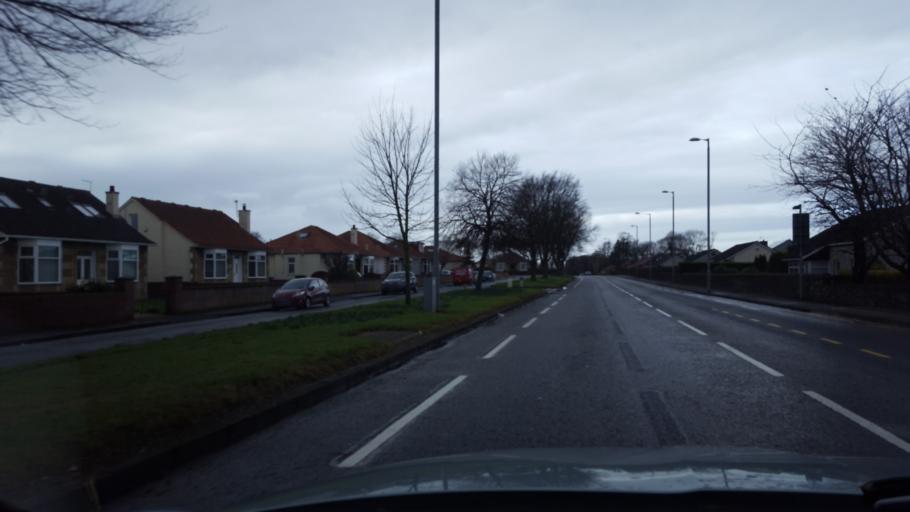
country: GB
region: Scotland
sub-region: South Ayrshire
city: Prestwick
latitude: 55.4556
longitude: -4.6012
